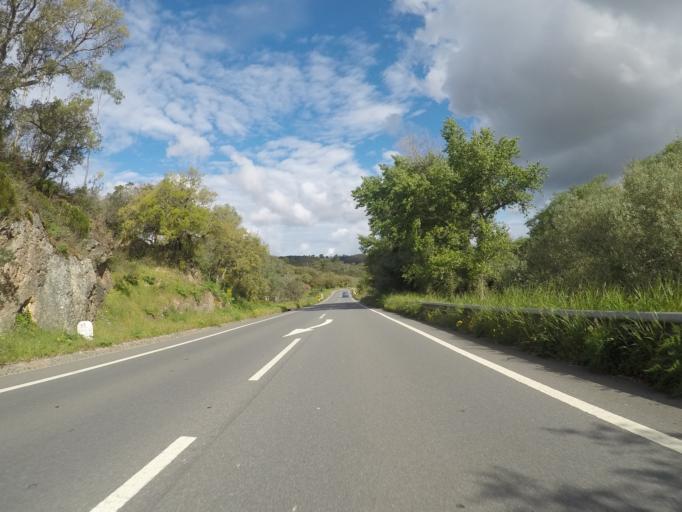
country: PT
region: Faro
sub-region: Aljezur
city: Aljezur
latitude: 37.2968
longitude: -8.7984
